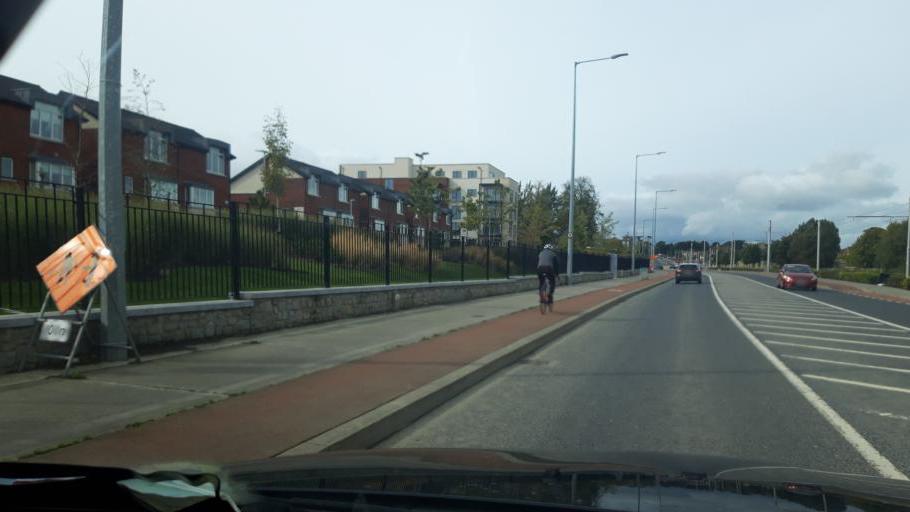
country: IE
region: Leinster
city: Foxrock
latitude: 53.2587
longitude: -6.2002
